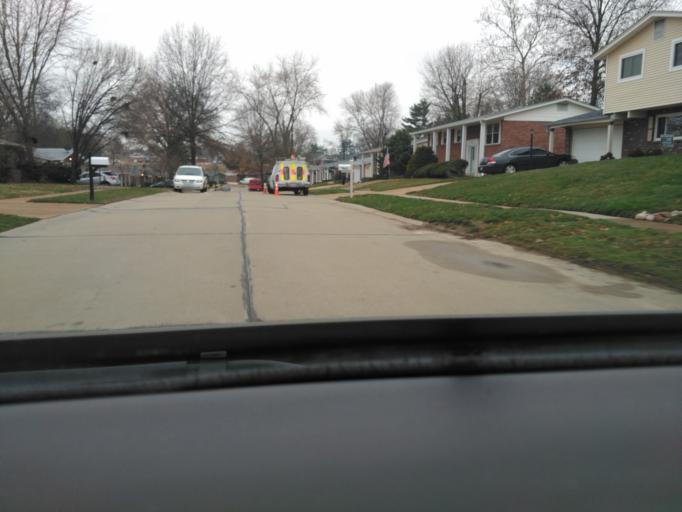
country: US
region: Missouri
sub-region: Saint Louis County
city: Concord
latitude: 38.5072
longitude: -90.3659
